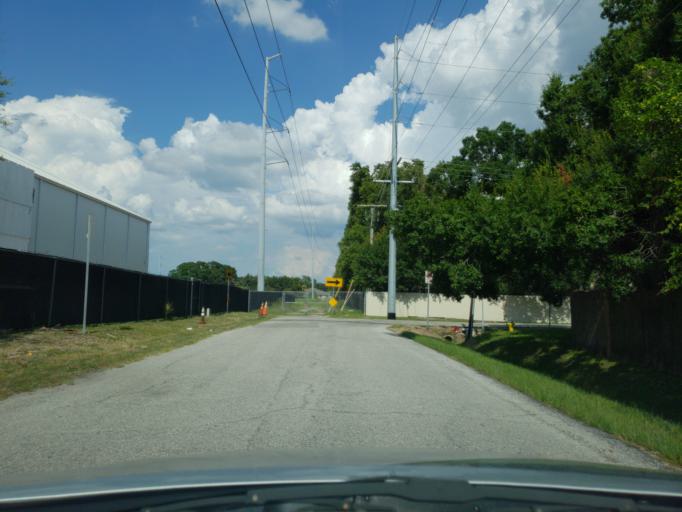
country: US
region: Florida
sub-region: Hillsborough County
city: Egypt Lake-Leto
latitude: 27.9774
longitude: -82.4962
